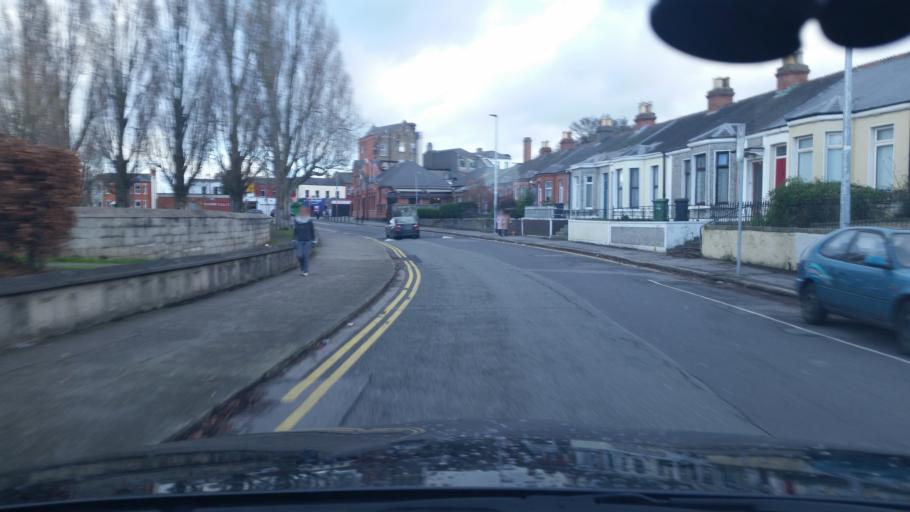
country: IE
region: Leinster
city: Drumcondra
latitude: 53.3679
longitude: -6.2575
